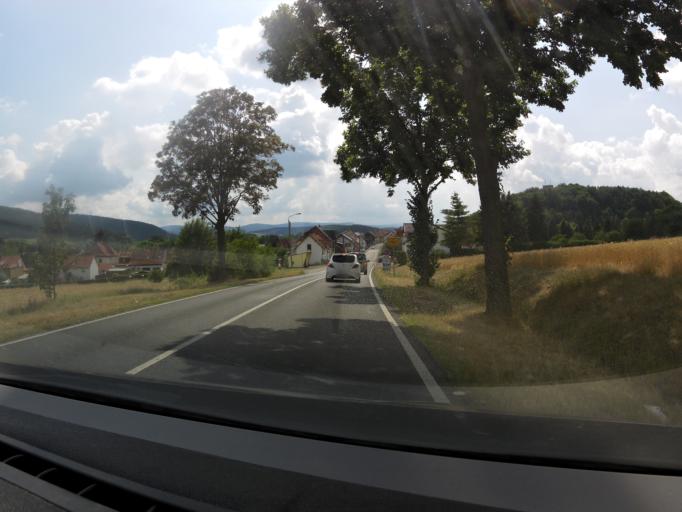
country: DE
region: Thuringia
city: Plaue
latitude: 50.7822
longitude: 10.9018
